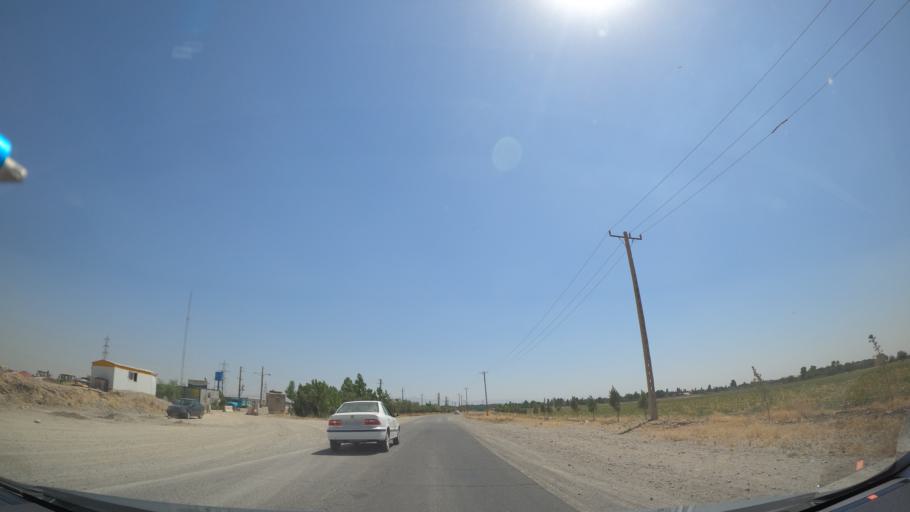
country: IR
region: Alborz
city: Hashtgerd
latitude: 35.9194
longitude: 50.7381
